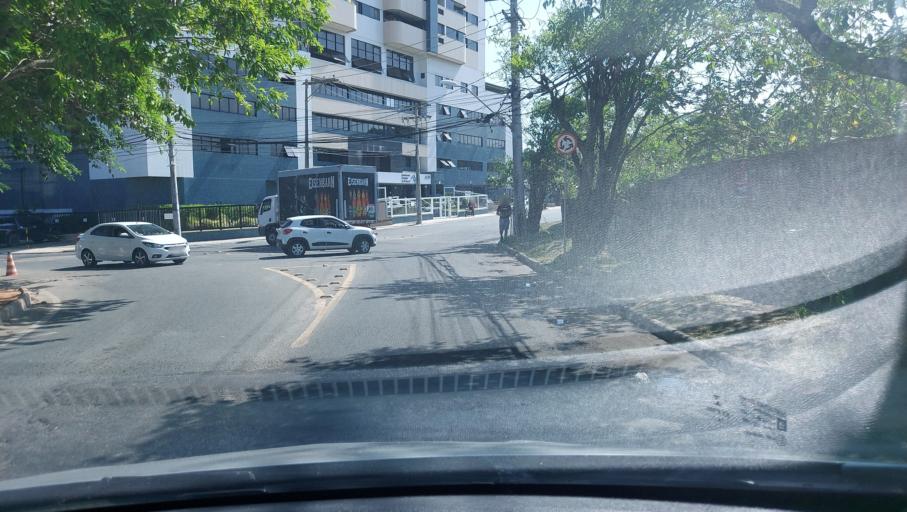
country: BR
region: Bahia
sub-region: Salvador
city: Salvador
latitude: -12.9779
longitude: -38.4422
